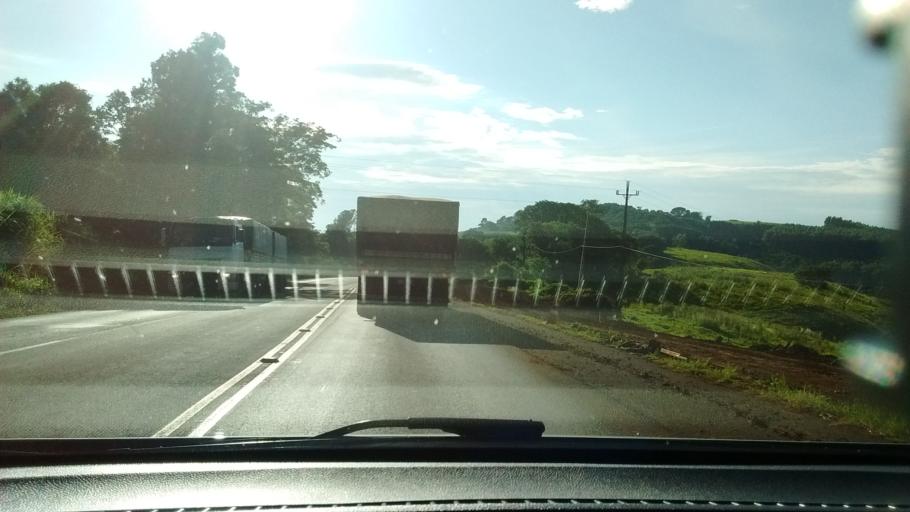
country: BR
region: Parana
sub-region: Cascavel
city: Cascavel
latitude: -25.2015
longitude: -53.6002
